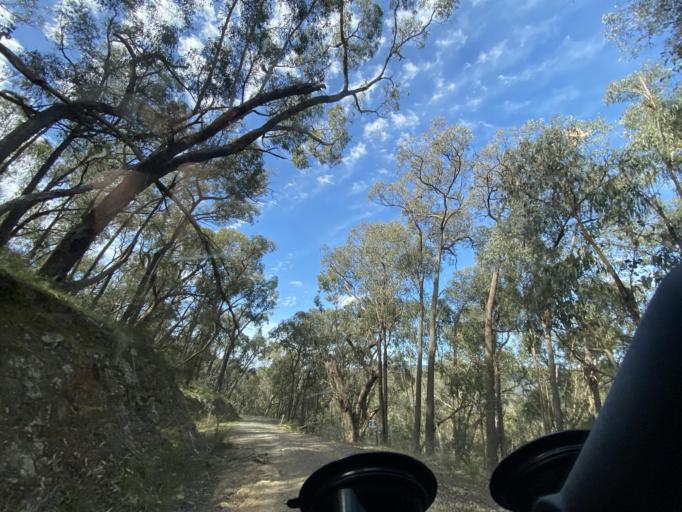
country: AU
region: Victoria
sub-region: Mansfield
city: Mansfield
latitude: -36.8001
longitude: 146.1119
